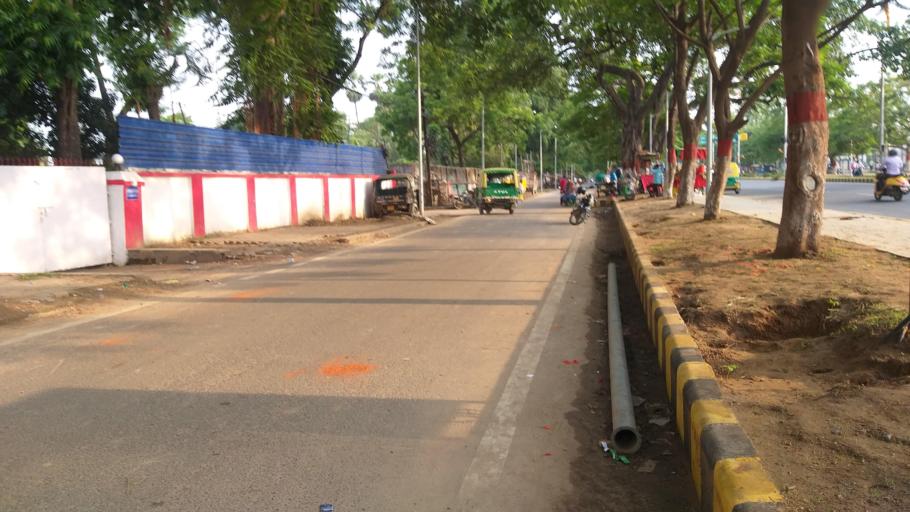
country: IN
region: Bihar
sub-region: Patna
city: Patna
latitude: 25.6053
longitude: 85.1282
